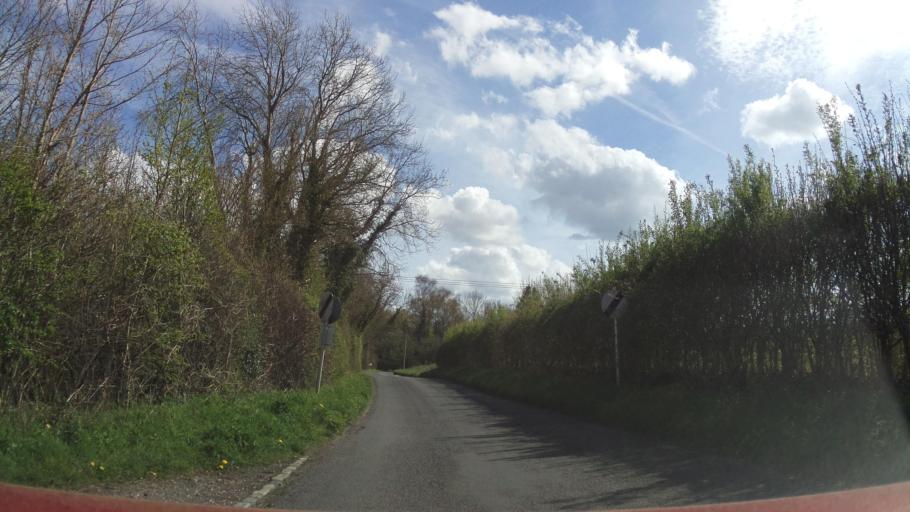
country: GB
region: England
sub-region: Hampshire
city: Andover
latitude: 51.1728
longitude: -1.4847
